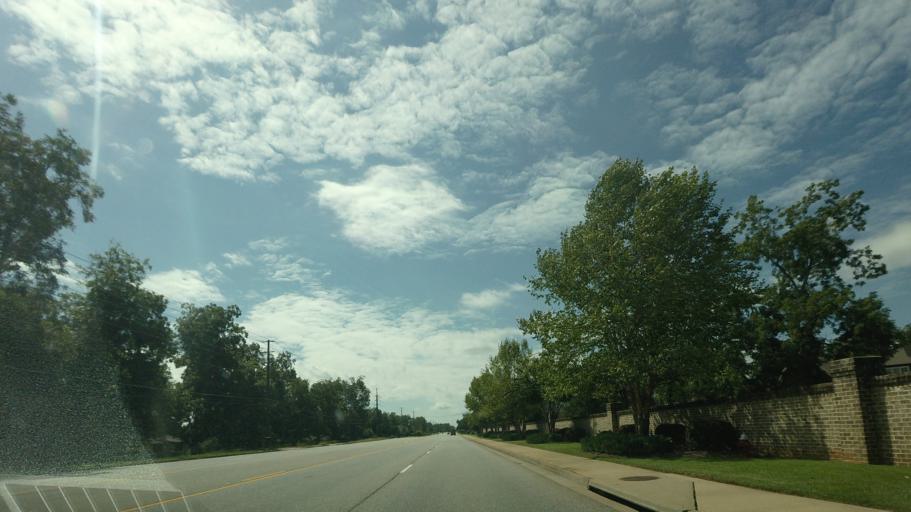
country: US
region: Georgia
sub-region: Houston County
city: Centerville
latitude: 32.5681
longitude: -83.6913
